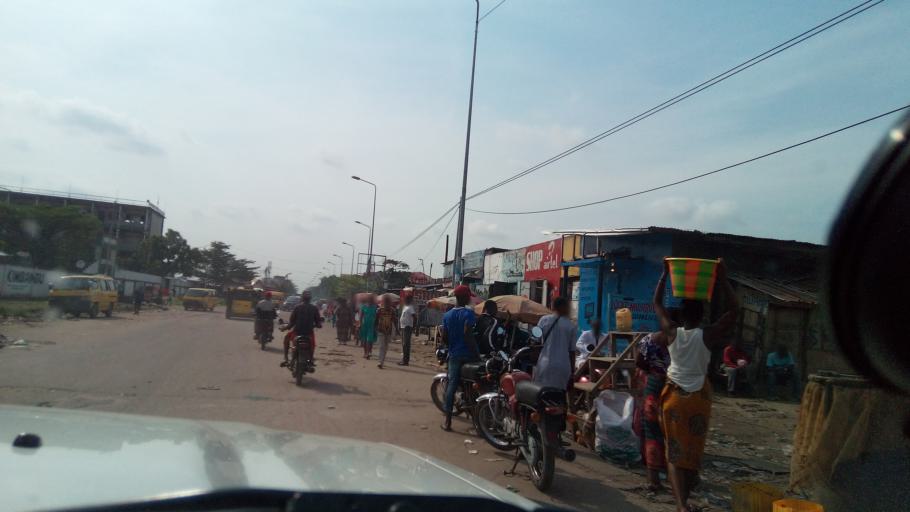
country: CD
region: Kinshasa
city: Kinshasa
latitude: -4.3481
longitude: 15.3161
